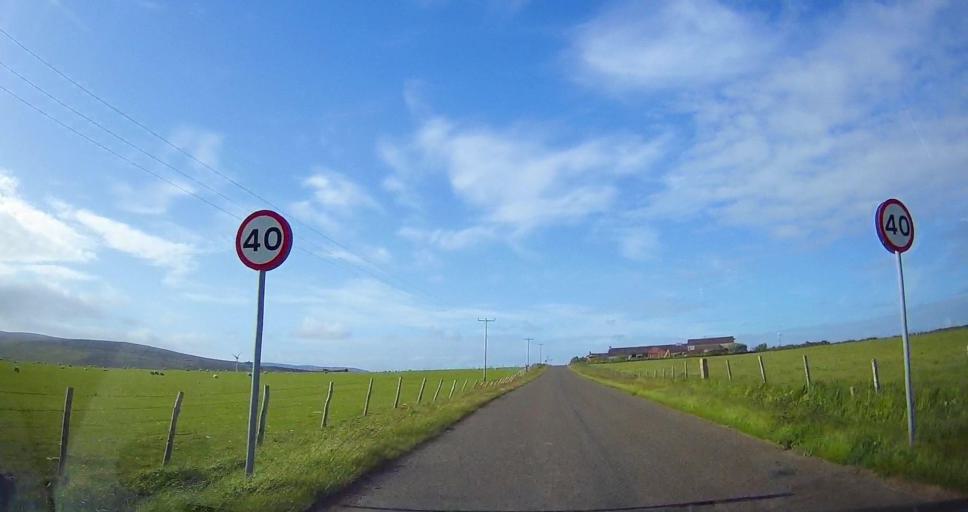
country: GB
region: Scotland
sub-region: Orkney Islands
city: Stromness
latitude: 58.8137
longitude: -3.2020
